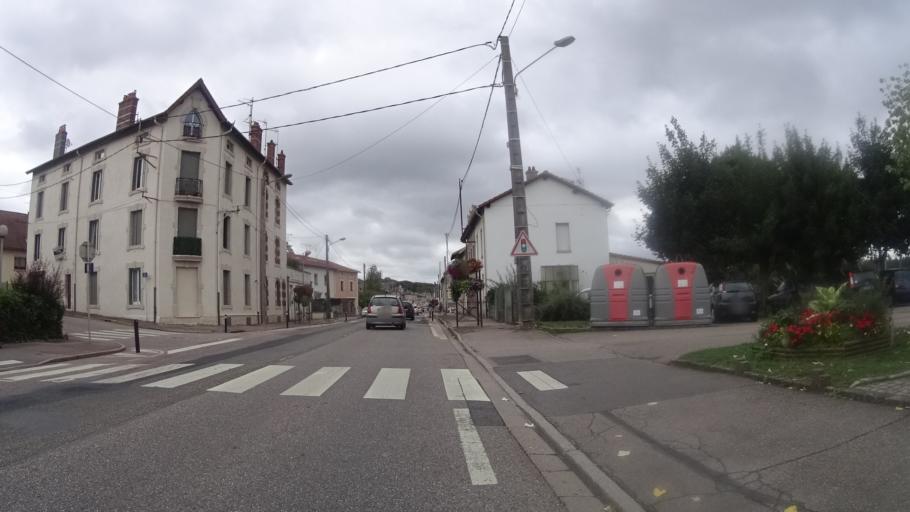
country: FR
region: Lorraine
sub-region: Departement de Meurthe-et-Moselle
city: Varangeville
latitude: 48.6349
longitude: 6.3176
